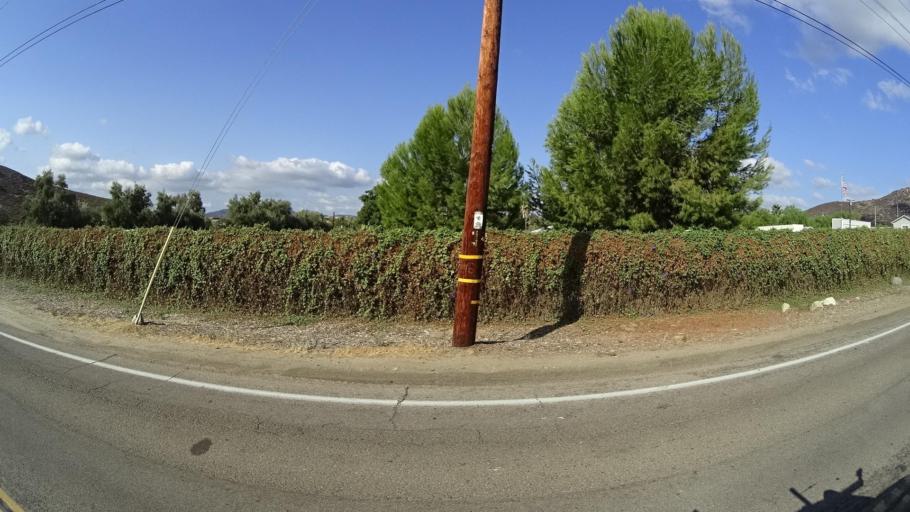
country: US
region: California
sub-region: San Diego County
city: Eucalyptus Hills
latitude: 32.8613
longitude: -116.9548
